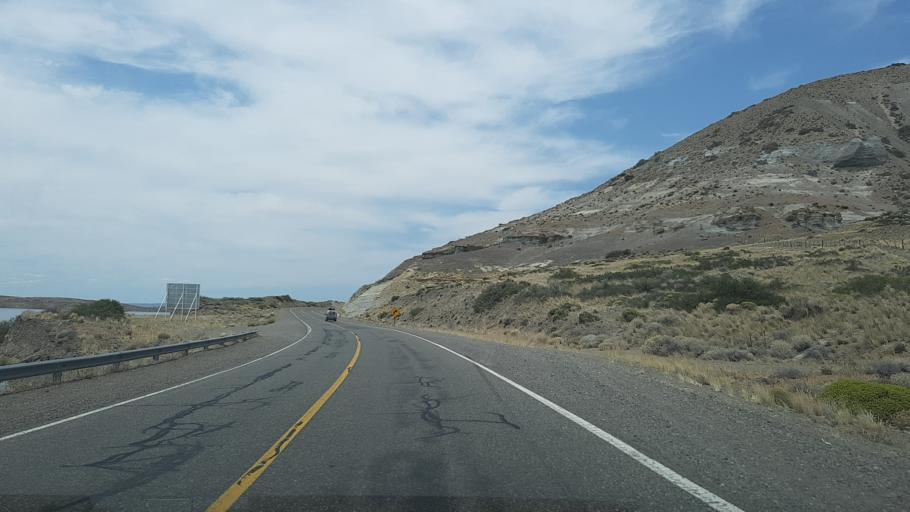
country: AR
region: Neuquen
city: Junin de los Andes
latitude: -40.4589
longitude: -70.6630
